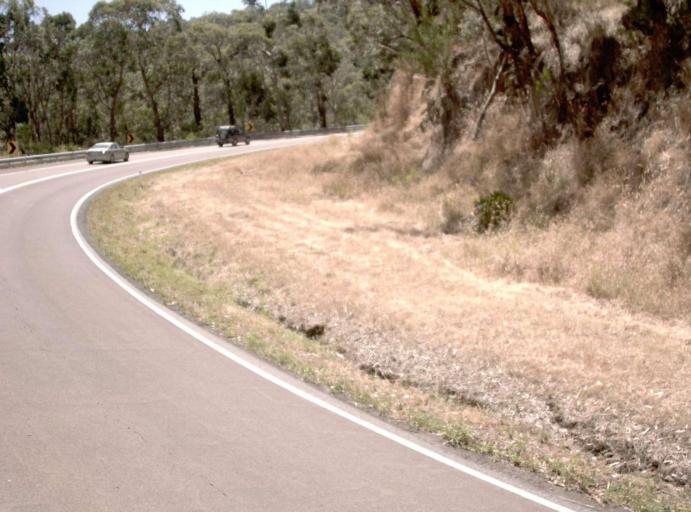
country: AU
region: Victoria
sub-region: Yarra Ranges
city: Ferny Creek
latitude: -37.8874
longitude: 145.3237
